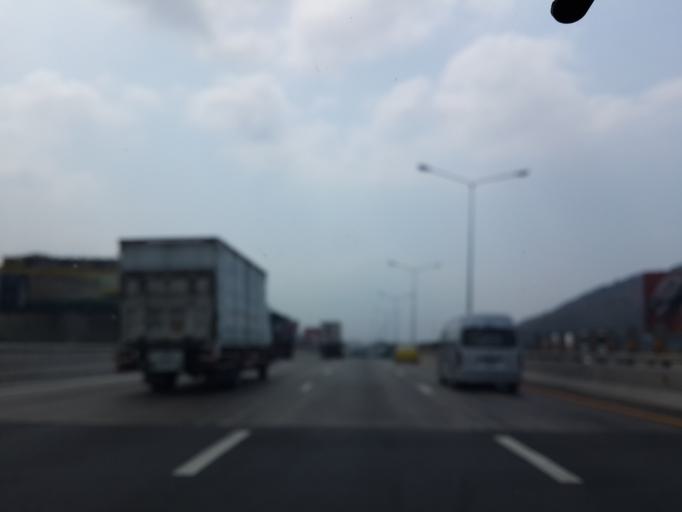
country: TH
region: Chon Buri
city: Chon Buri
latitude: 13.2832
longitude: 100.9911
